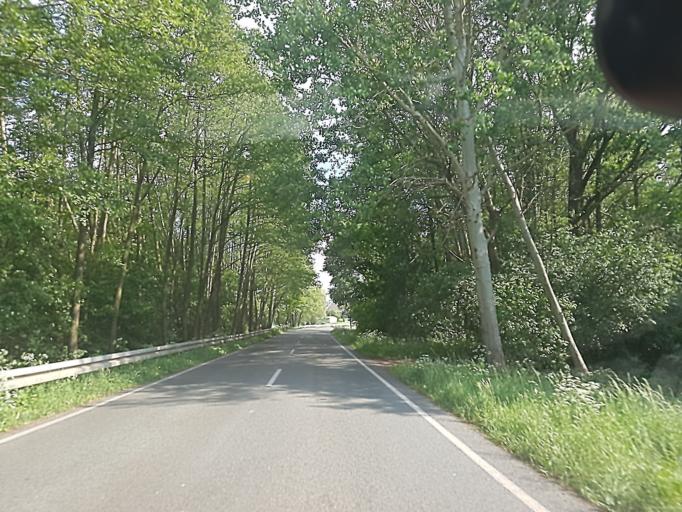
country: DE
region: Saxony-Anhalt
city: Rodleben
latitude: 52.0164
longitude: 12.2303
